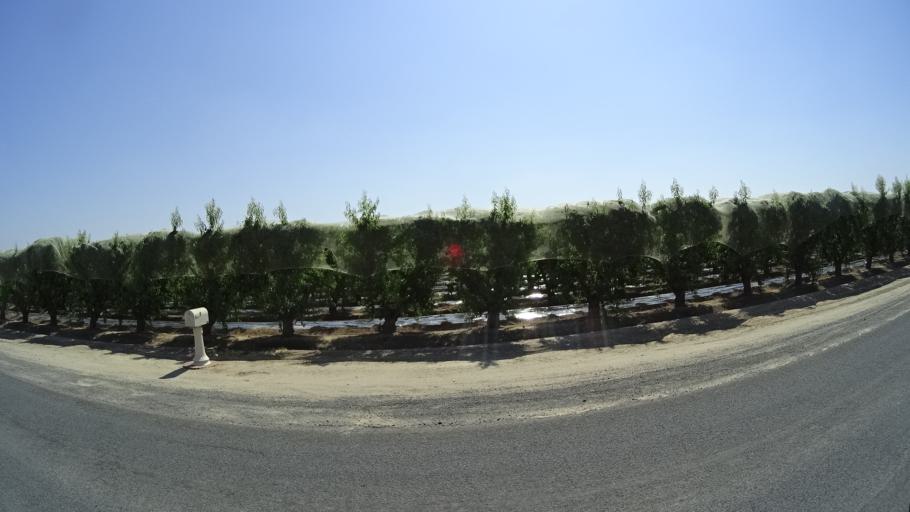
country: US
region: California
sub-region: Fresno County
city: Kingsburg
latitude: 36.4499
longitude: -119.5285
